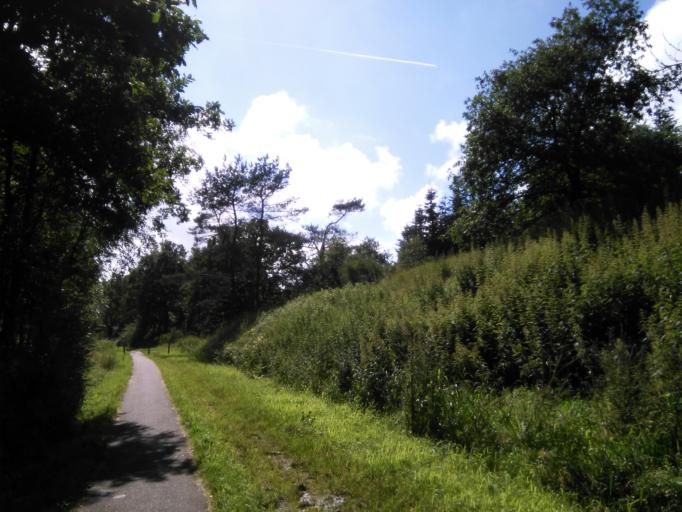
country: DK
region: Central Jutland
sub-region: Silkeborg Kommune
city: Virklund
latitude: 56.0606
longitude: 9.4743
